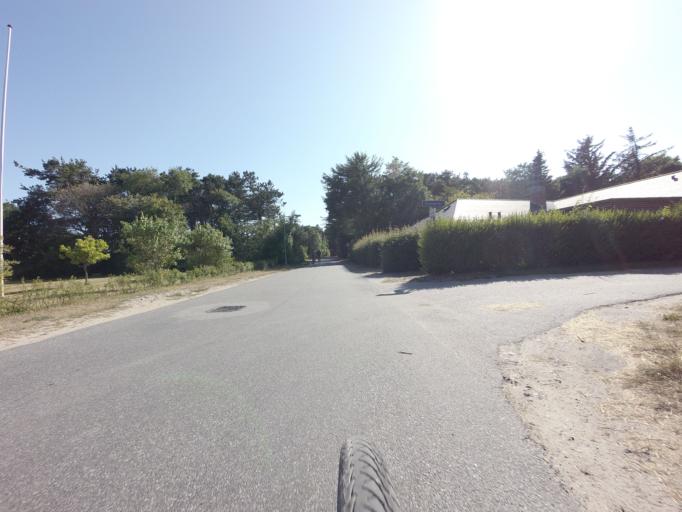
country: DK
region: North Denmark
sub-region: Laeso Kommune
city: Byrum
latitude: 57.2873
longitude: 10.9206
